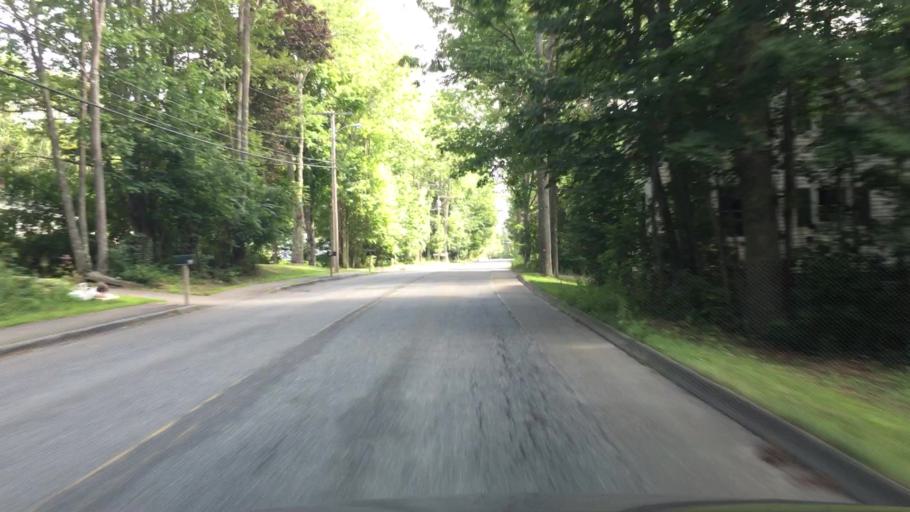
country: US
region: Maine
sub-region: Penobscot County
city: Hampden
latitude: 44.7346
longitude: -68.8596
